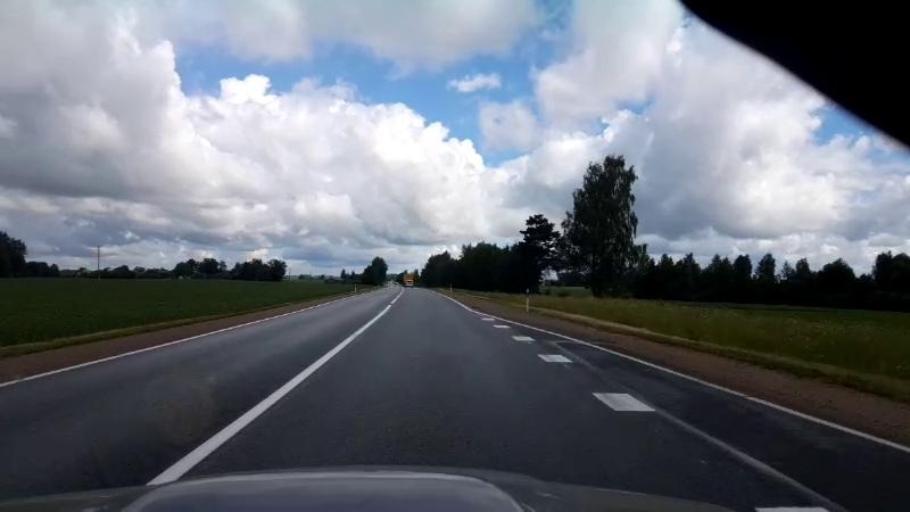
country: LV
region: Bauskas Rajons
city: Bauska
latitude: 56.4891
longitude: 24.1770
